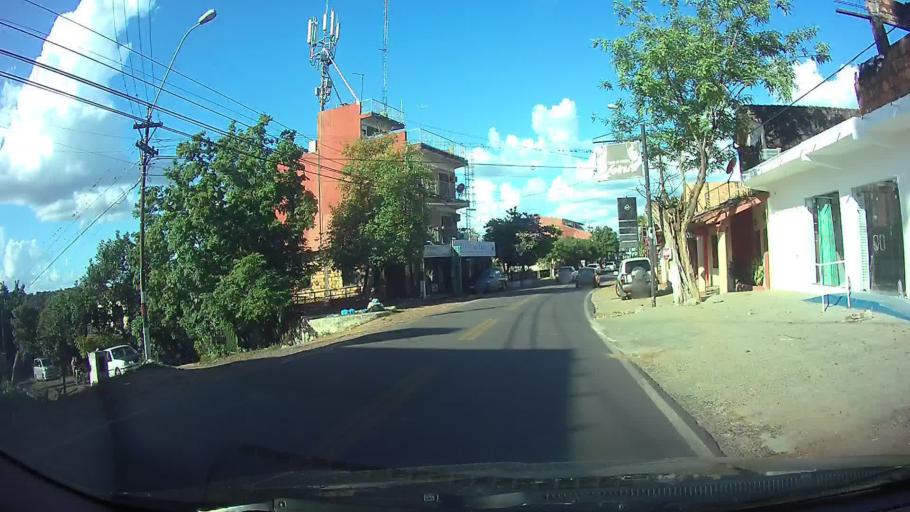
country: PY
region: Central
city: Aregua
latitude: -25.3161
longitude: -57.3881
